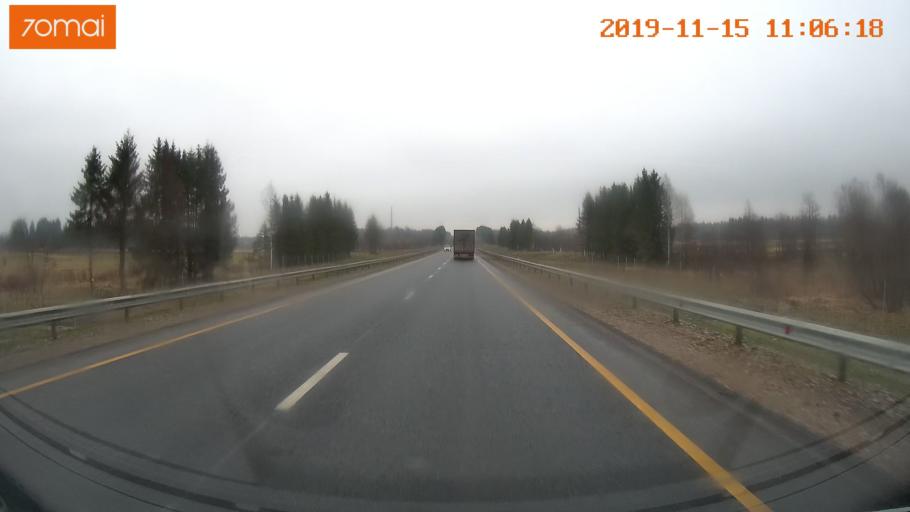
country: RU
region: Vologda
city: Chebsara
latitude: 59.1190
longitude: 39.0244
